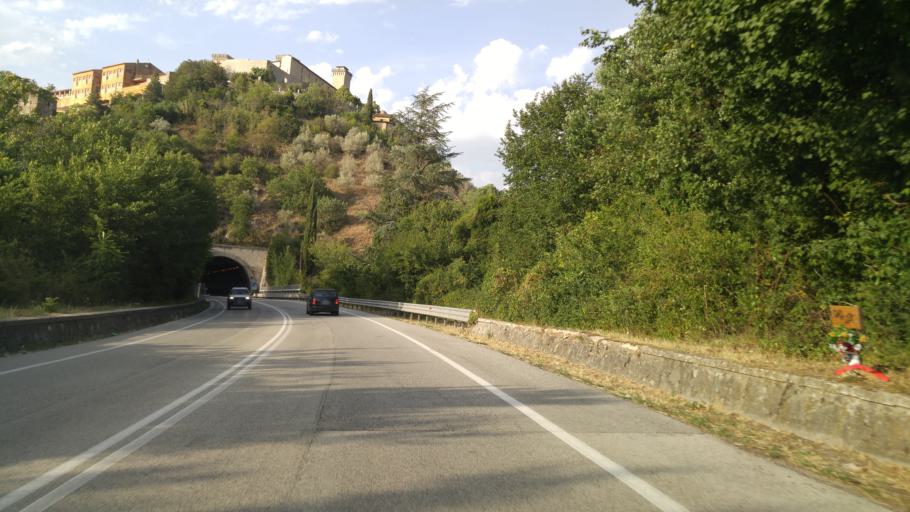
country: IT
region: Umbria
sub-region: Provincia di Perugia
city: Spoleto
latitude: 42.7306
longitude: 12.7398
